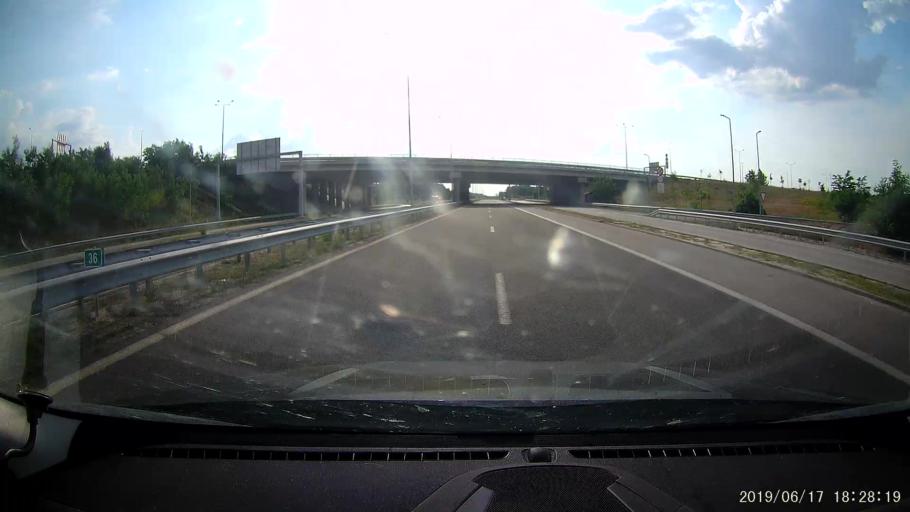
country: BG
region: Khaskovo
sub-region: Obshtina Dimitrovgrad
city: Dimitrovgrad
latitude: 42.0221
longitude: 25.5826
